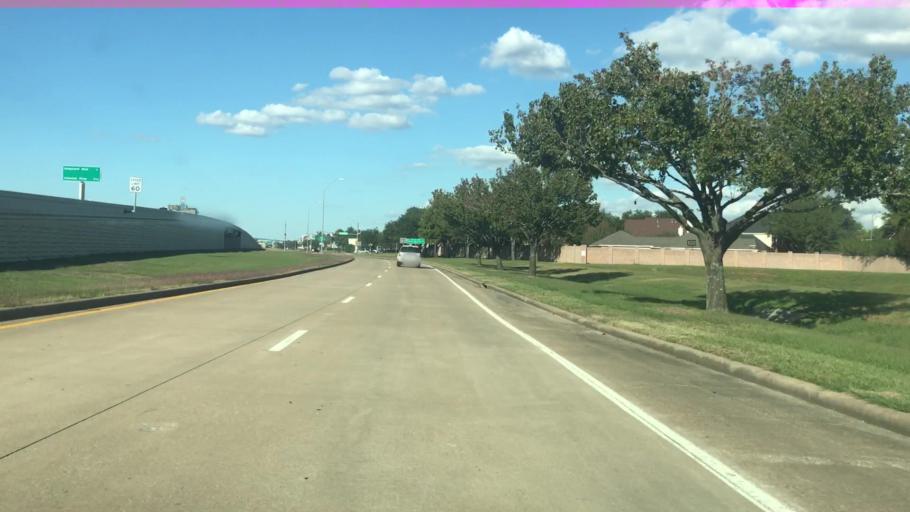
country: US
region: Texas
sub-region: Fort Bend County
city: Cinco Ranch
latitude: 29.7542
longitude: -95.7759
